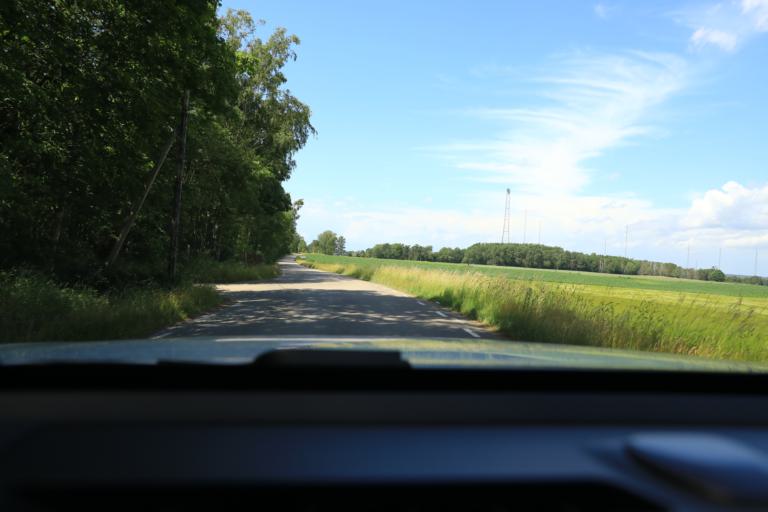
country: SE
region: Halland
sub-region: Varbergs Kommun
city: Tvaaker
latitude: 57.0956
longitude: 12.3922
